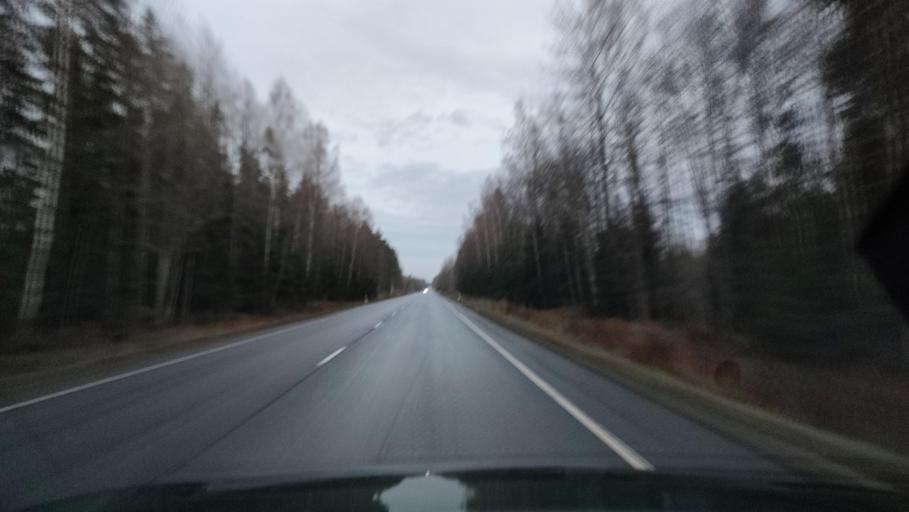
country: FI
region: Ostrobothnia
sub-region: Vaasa
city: Ristinummi
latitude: 62.9985
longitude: 21.7648
